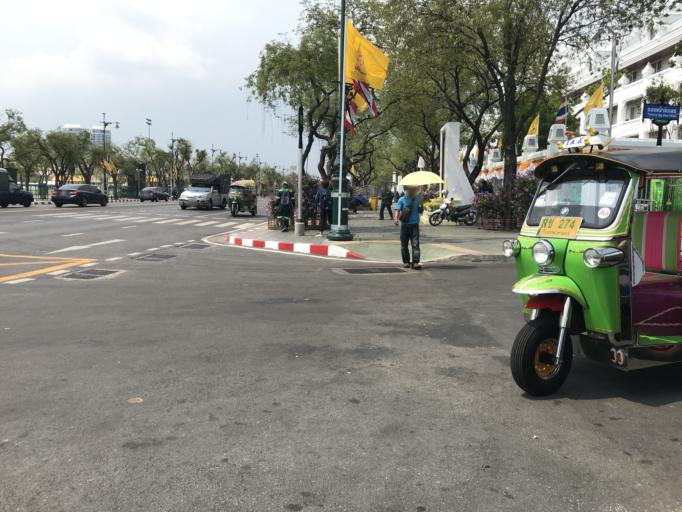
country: TH
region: Bangkok
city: Bangkok
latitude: 13.7531
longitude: 100.4938
